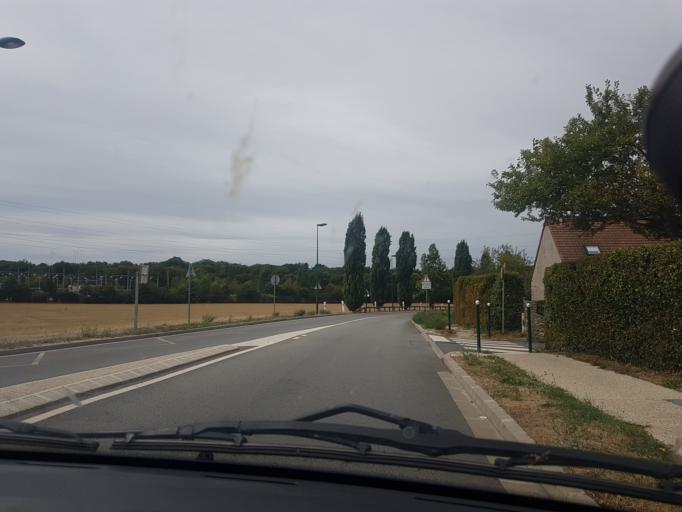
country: FR
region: Ile-de-France
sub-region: Departement des Yvelines
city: Plaisir
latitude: 48.8071
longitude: 1.9472
